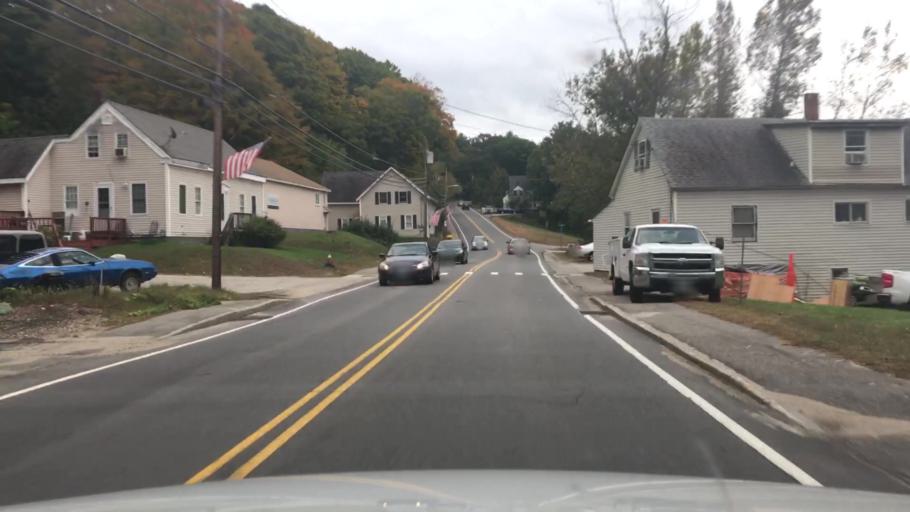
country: US
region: New Hampshire
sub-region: Strafford County
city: New Durham
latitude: 43.4651
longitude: -71.2296
